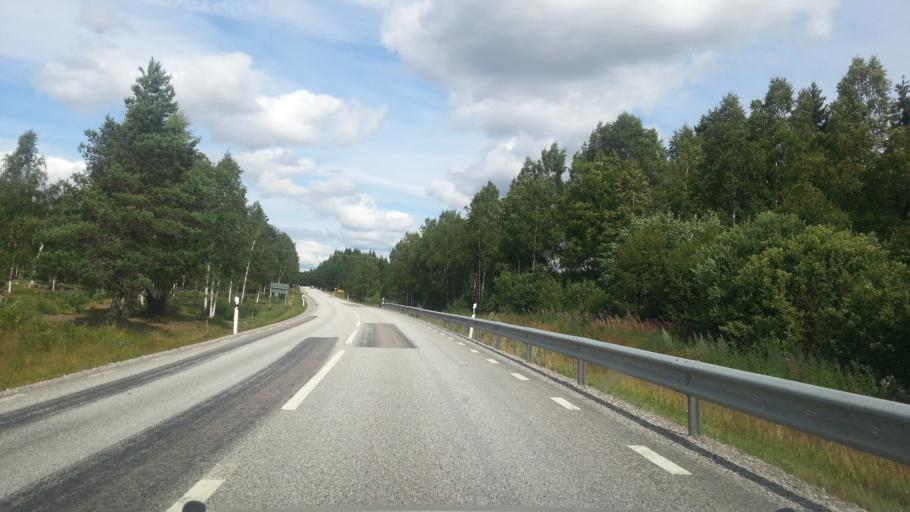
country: SE
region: Vaestmanland
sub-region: Skinnskattebergs Kommun
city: Skinnskatteberg
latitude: 59.7778
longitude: 15.5455
